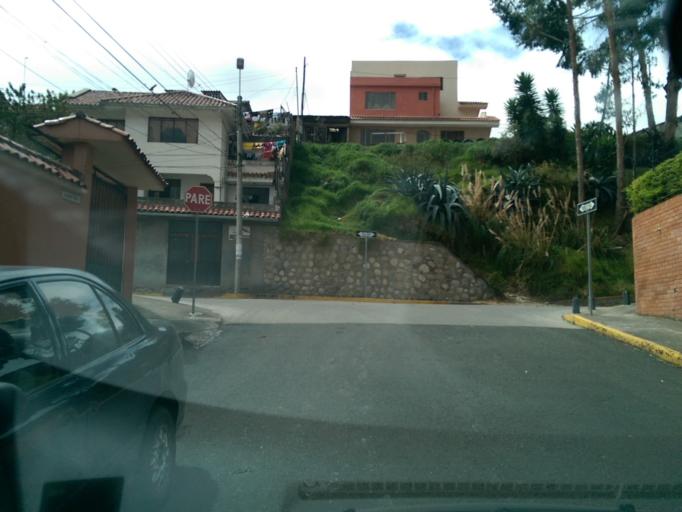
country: EC
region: Azuay
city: Cuenca
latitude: -2.9116
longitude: -79.0115
